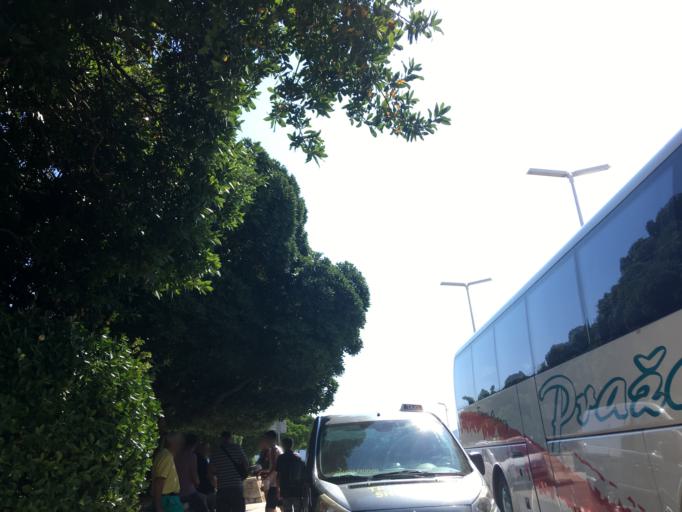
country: HR
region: Zadarska
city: Zadar
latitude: 44.1178
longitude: 15.2208
